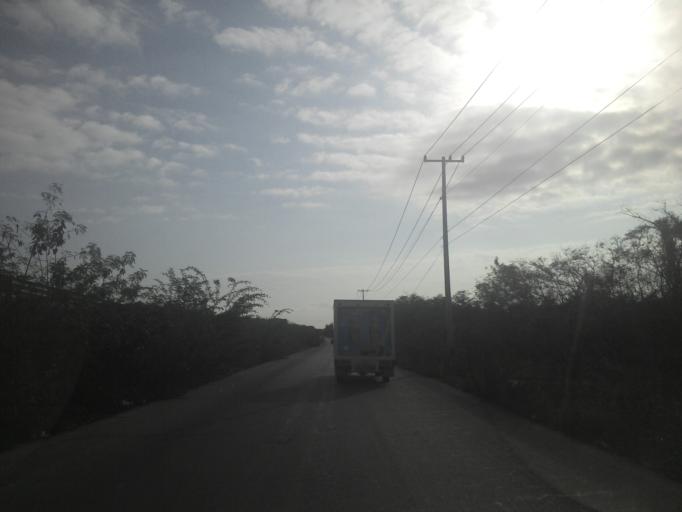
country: MX
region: Yucatan
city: Valladolid
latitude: 20.7250
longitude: -88.2013
